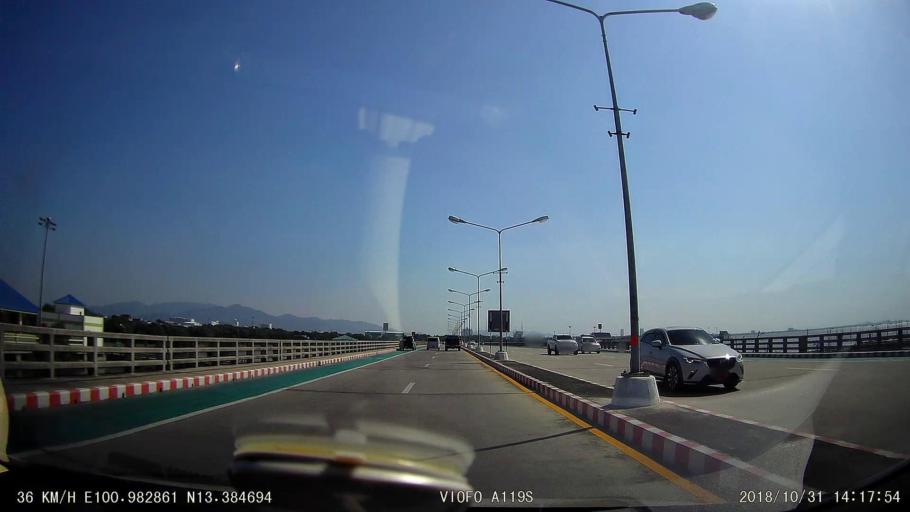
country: TH
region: Chon Buri
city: Chon Buri
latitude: 13.3846
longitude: 100.9827
